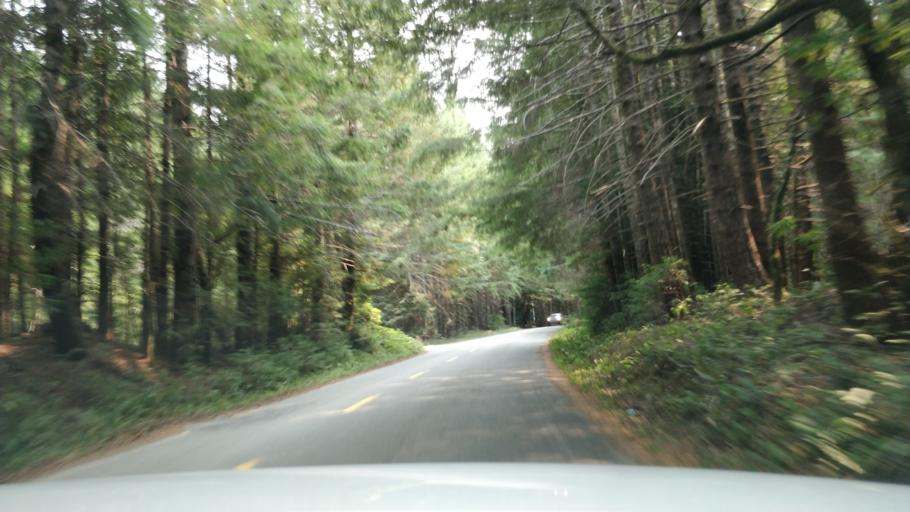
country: US
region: California
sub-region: Humboldt County
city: Westhaven-Moonstone
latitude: 41.2488
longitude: -123.9838
